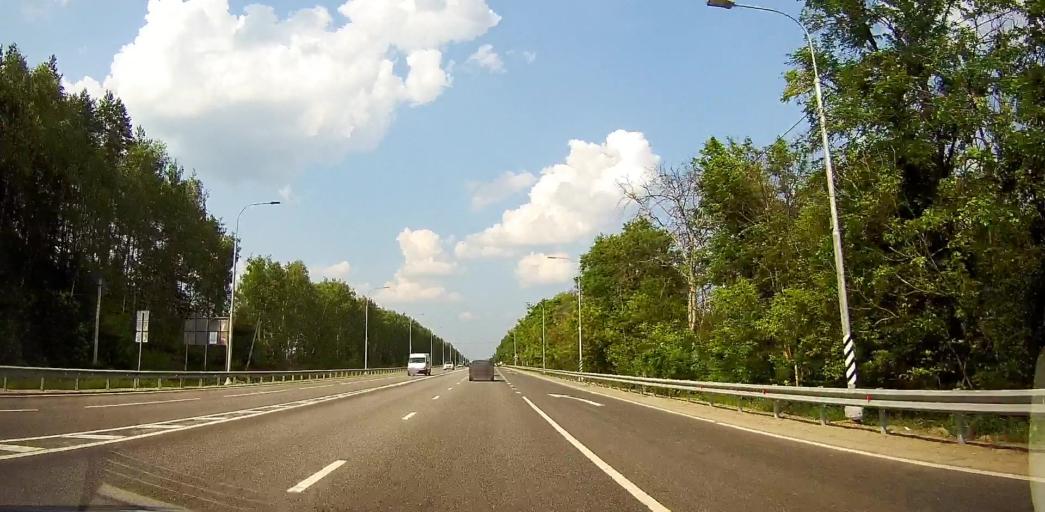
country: RU
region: Moskovskaya
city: Mikhnevo
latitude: 55.0795
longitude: 37.9528
